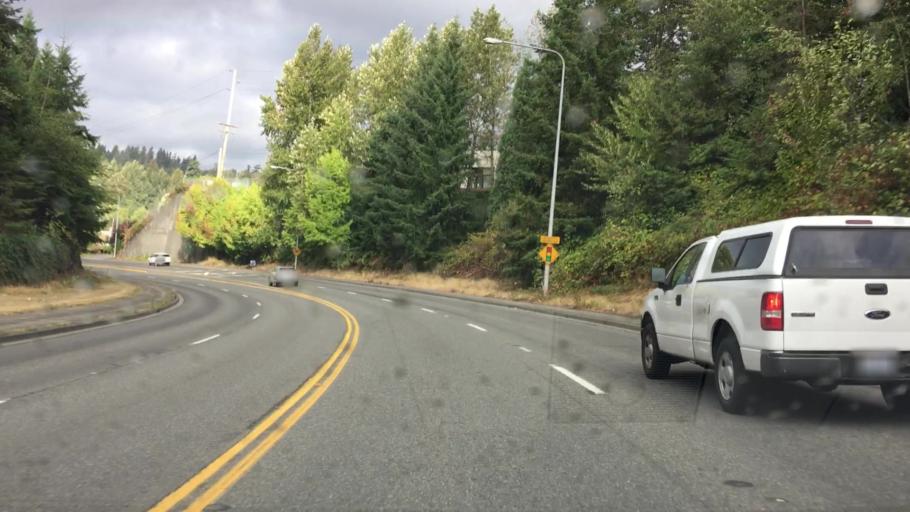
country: US
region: Washington
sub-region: King County
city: Woodinville
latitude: 47.7684
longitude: -122.1514
